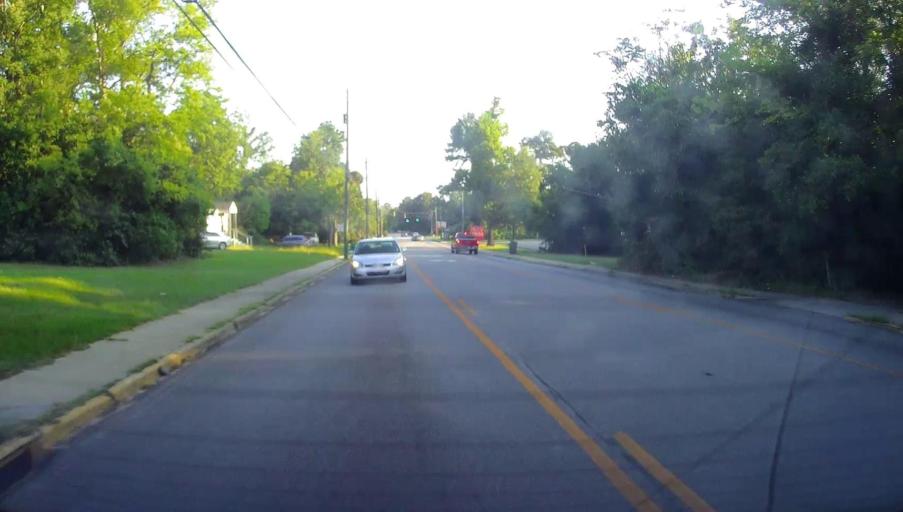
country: US
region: Georgia
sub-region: Bibb County
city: Macon
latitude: 32.8483
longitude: -83.6879
